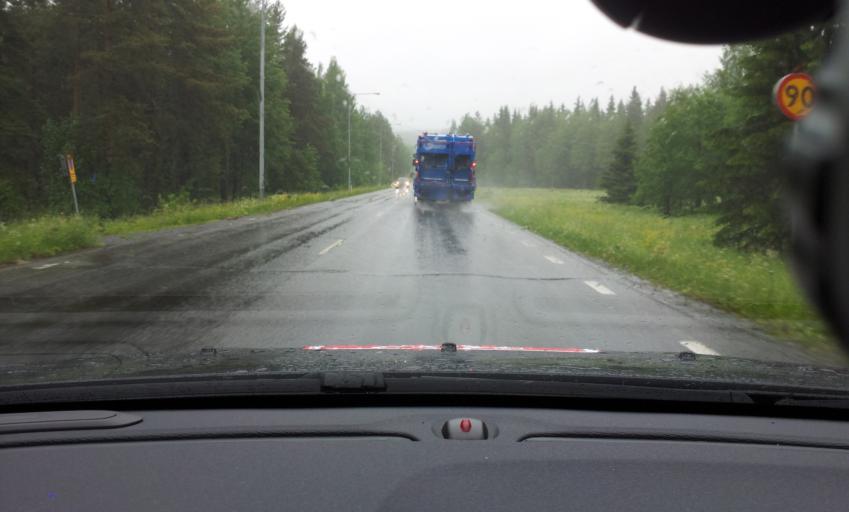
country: SE
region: Jaemtland
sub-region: OEstersunds Kommun
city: Ostersund
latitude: 63.1960
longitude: 14.6664
